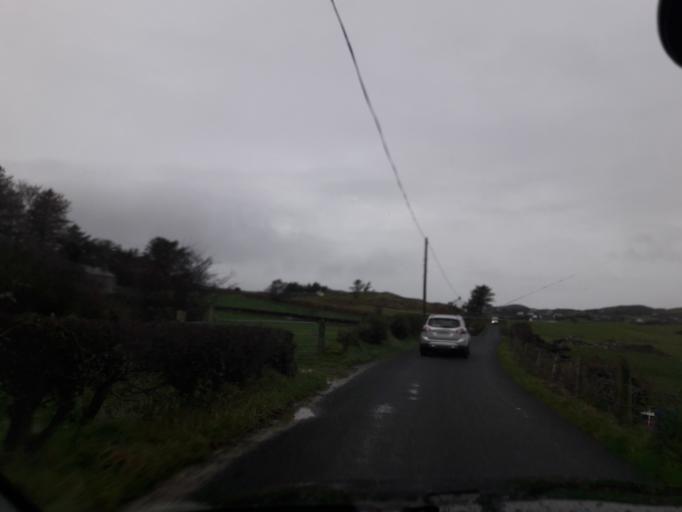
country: IE
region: Ulster
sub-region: County Donegal
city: Buncrana
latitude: 55.2413
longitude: -7.6215
